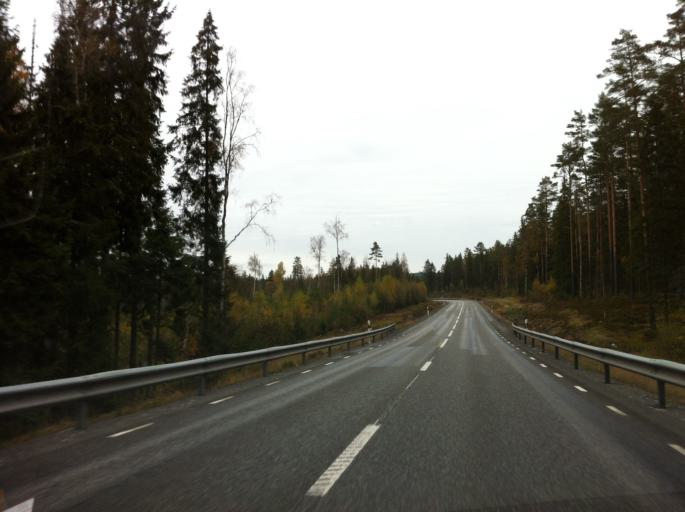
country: SE
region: OErebro
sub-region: Ljusnarsbergs Kommun
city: Kopparberg
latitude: 59.9327
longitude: 15.0232
